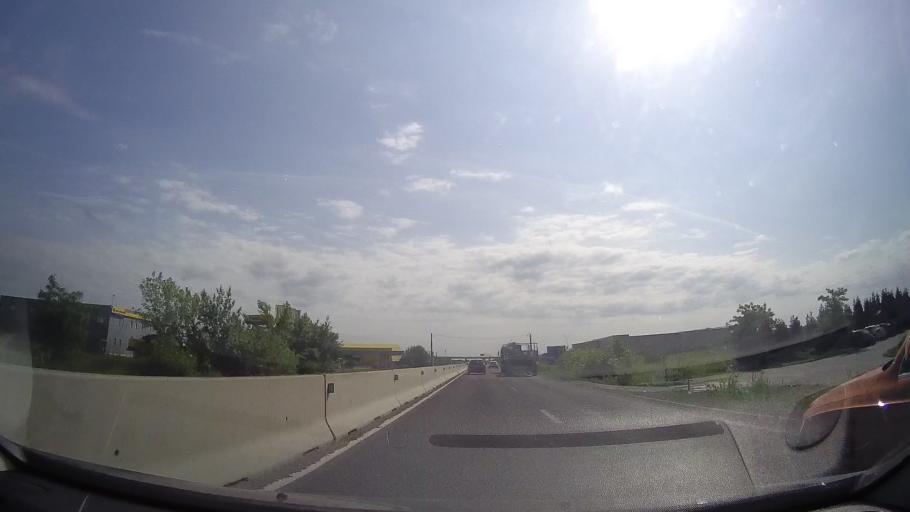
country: RO
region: Timis
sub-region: Comuna Ghiroda
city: Ghiroda
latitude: 45.7769
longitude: 21.3097
